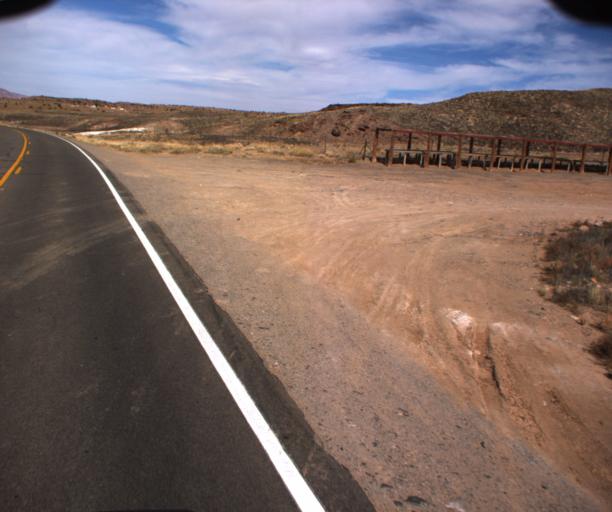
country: US
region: Arizona
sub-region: Navajo County
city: Kayenta
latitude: 36.8251
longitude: -110.2379
